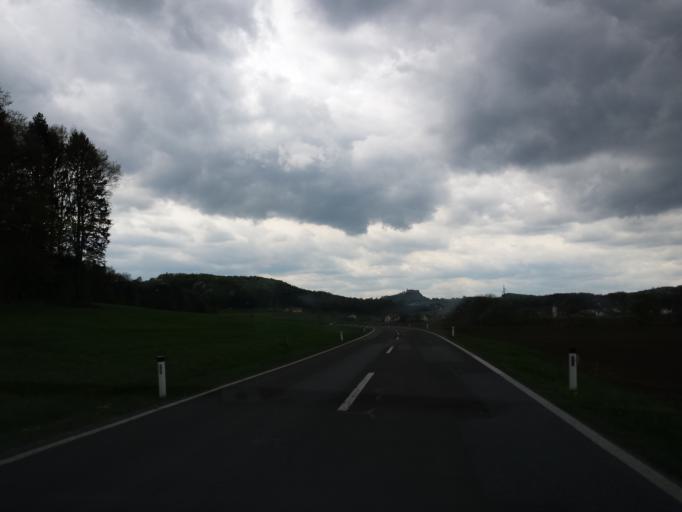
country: AT
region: Styria
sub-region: Politischer Bezirk Suedoststeiermark
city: Hatzendorf
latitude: 46.9861
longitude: 15.9878
